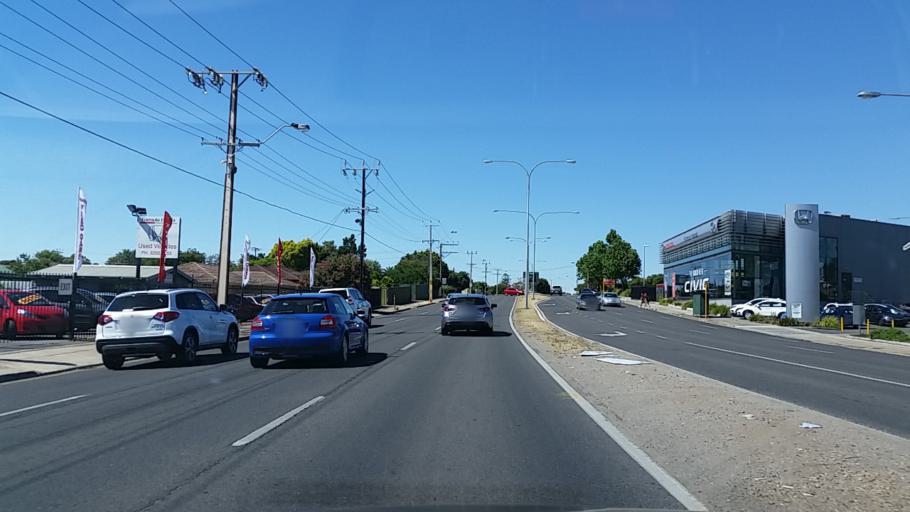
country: AU
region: South Australia
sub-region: Tea Tree Gully
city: Modbury
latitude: -34.8443
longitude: 138.6715
